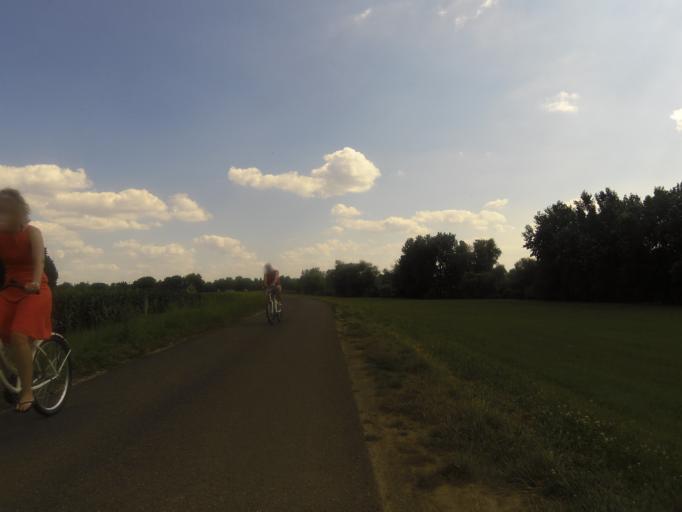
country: HU
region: Jasz-Nagykun-Szolnok
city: Tiszafured
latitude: 47.6162
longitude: 20.7256
